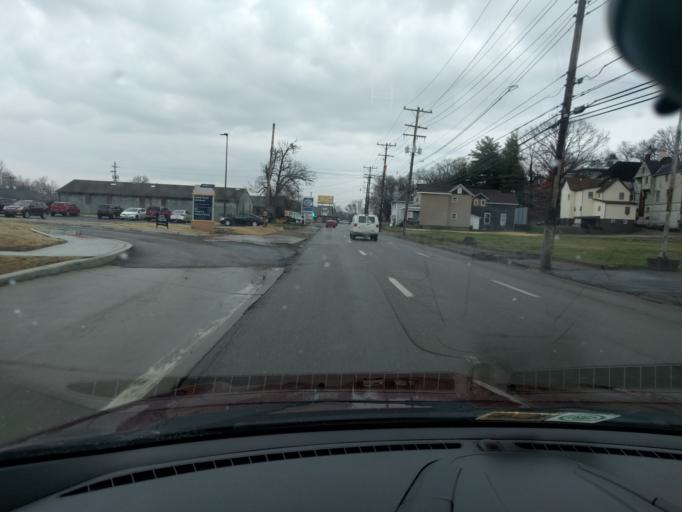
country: US
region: West Virginia
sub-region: Wood County
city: Parkersburg
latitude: 39.2721
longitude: -81.5569
